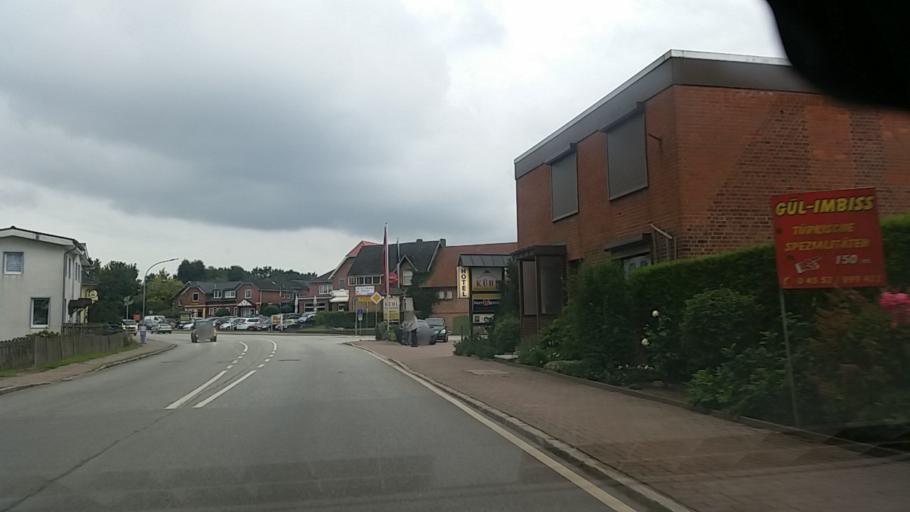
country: DE
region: Schleswig-Holstein
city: Leezen
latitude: 53.8687
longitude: 10.2530
